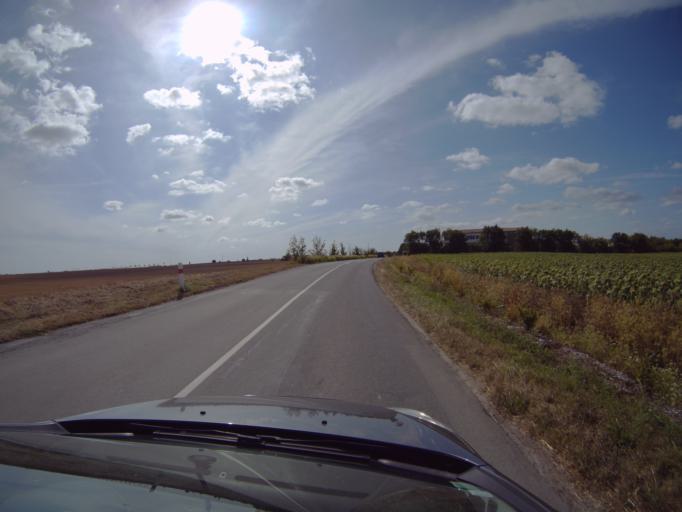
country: FR
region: Poitou-Charentes
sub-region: Departement des Deux-Sevres
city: Saint-Hilaire-la-Palud
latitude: 46.2593
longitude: -0.7033
